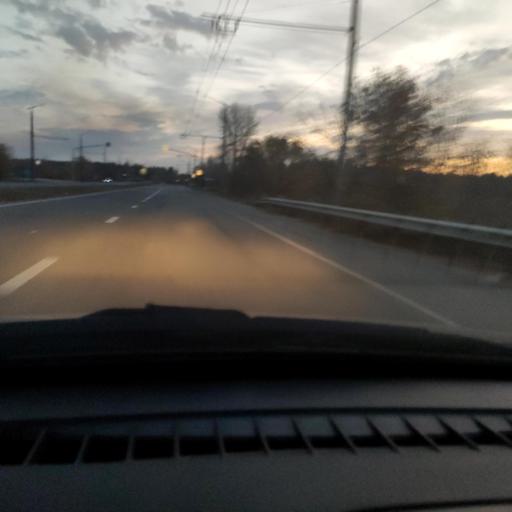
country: RU
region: Samara
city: Zhigulevsk
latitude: 53.5363
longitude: 49.5622
